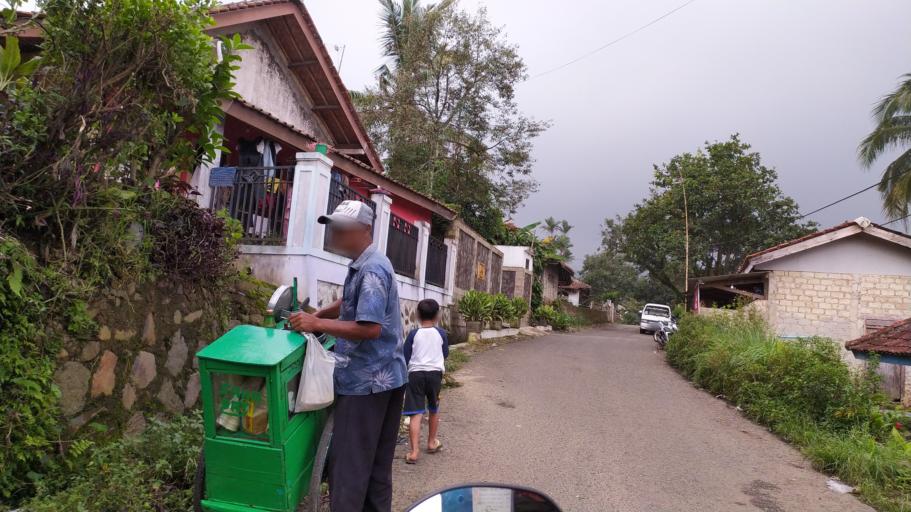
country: ID
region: West Java
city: Ciampea
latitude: -6.6514
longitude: 106.7063
